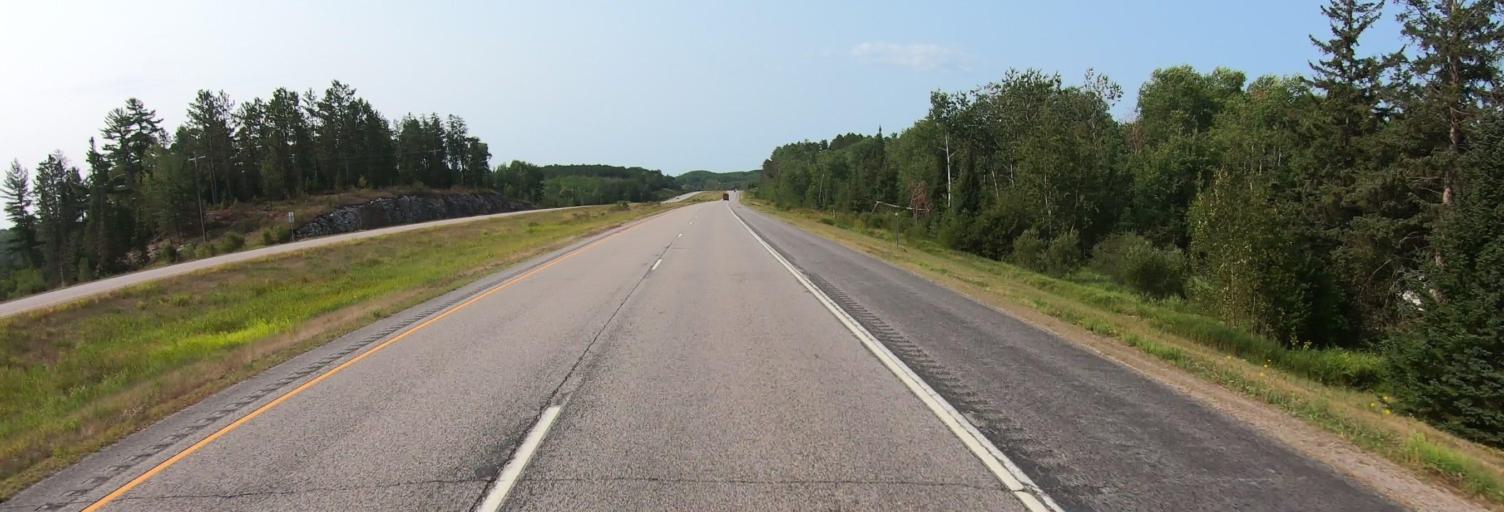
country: US
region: Minnesota
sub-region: Saint Louis County
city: Mountain Iron
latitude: 47.6970
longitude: -92.6467
